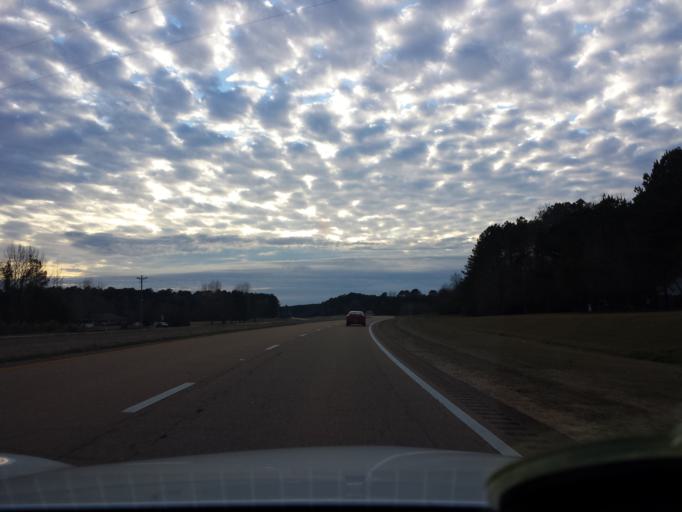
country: US
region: Mississippi
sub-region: Winston County
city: Louisville
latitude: 33.2587
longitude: -88.9514
